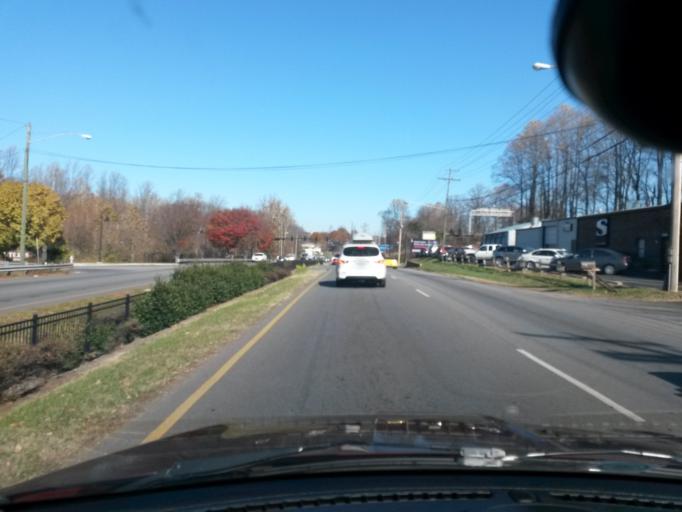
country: US
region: Virginia
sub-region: City of Lynchburg
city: West Lynchburg
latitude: 37.3544
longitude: -79.1826
